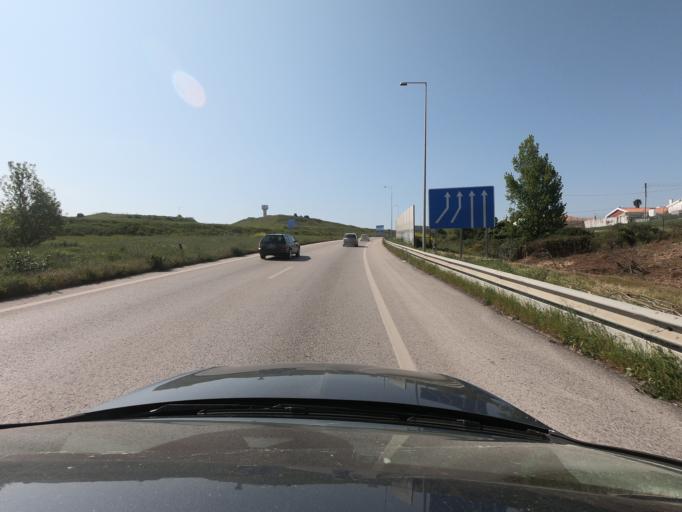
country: PT
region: Lisbon
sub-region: Sintra
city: Sintra
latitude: 38.8115
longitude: -9.3576
